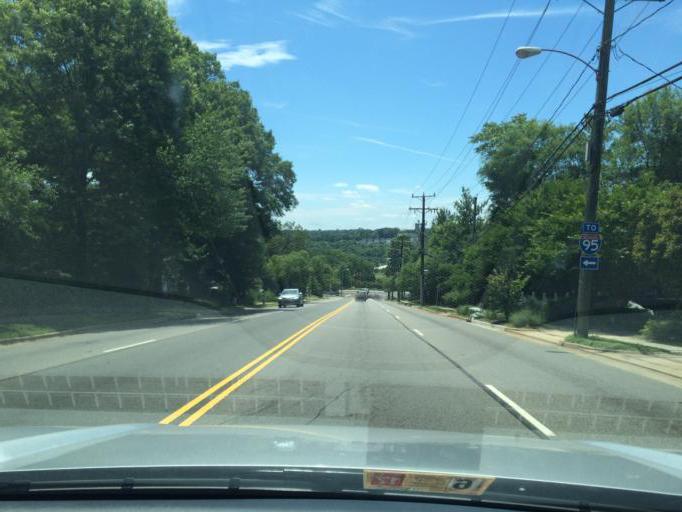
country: US
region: Virginia
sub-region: Fairfax County
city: Huntington
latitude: 38.8104
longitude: -77.0888
